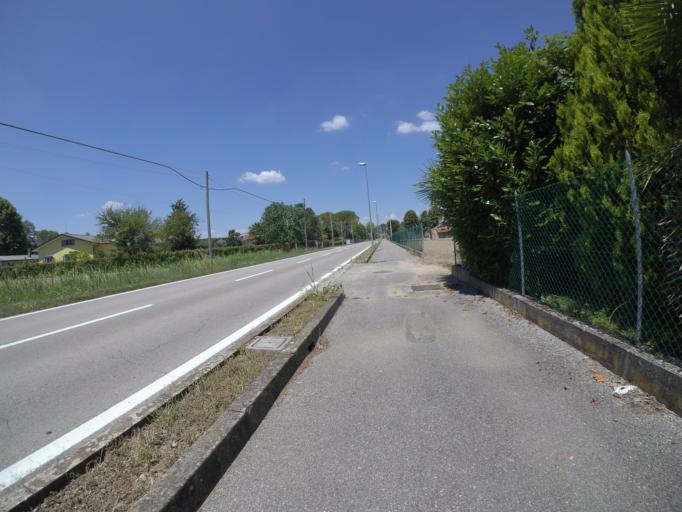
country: IT
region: Friuli Venezia Giulia
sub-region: Provincia di Udine
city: Rivignano
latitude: 45.8867
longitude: 13.0364
